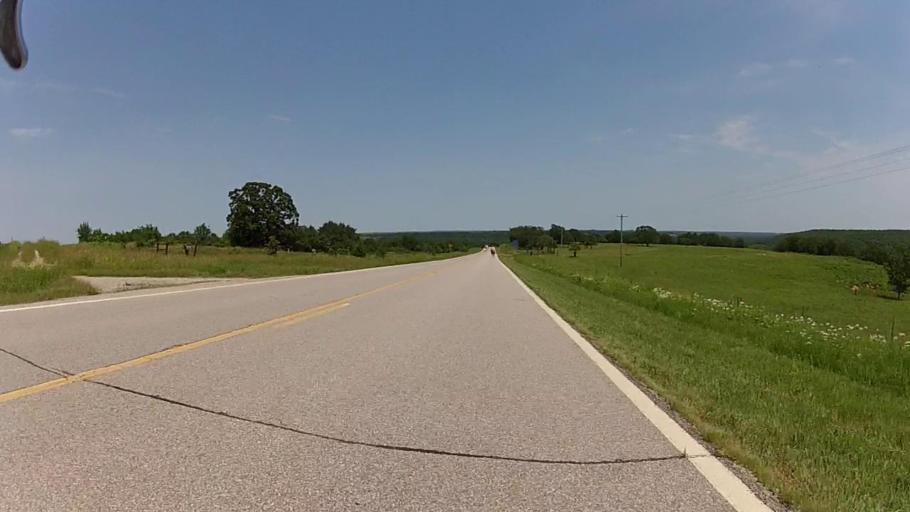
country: US
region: Kansas
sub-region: Chautauqua County
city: Sedan
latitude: 37.1166
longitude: -96.2402
